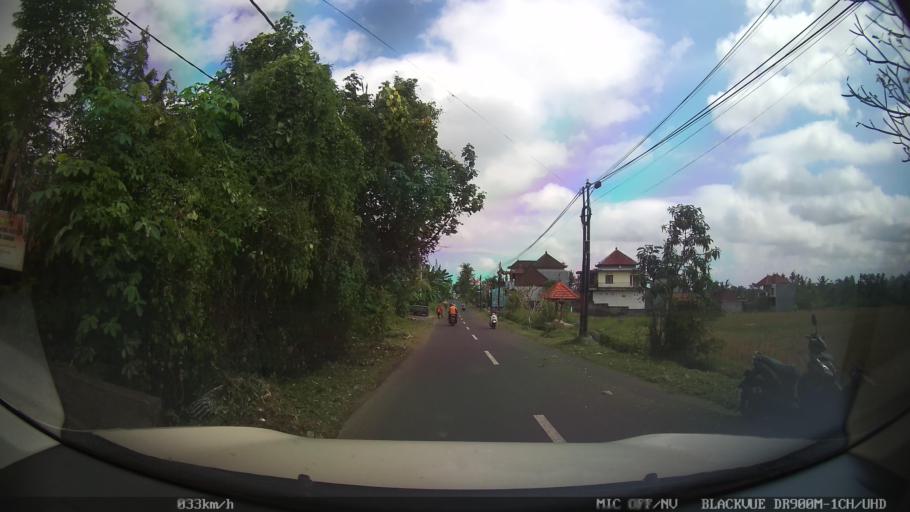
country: ID
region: Bali
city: Banjar Pesalakan
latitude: -8.5130
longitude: 115.3125
